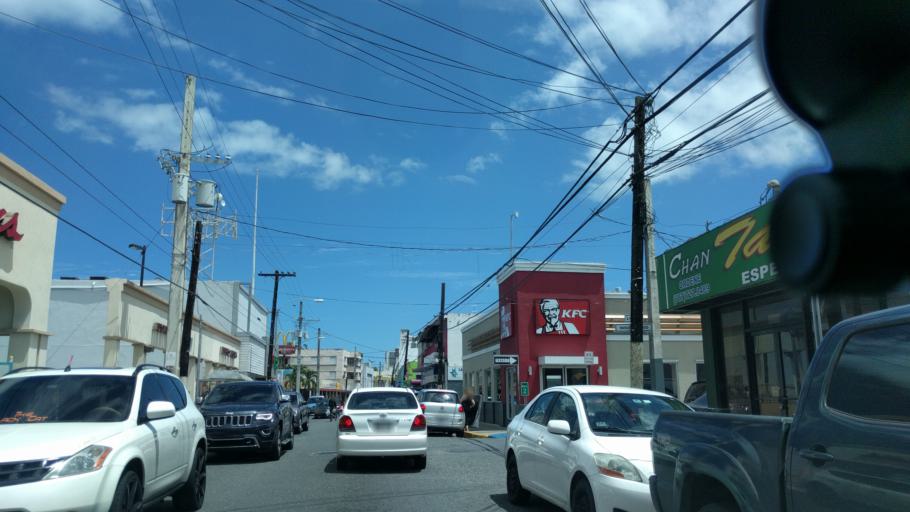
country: PR
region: San Juan
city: San Juan
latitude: 18.4510
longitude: -66.0553
